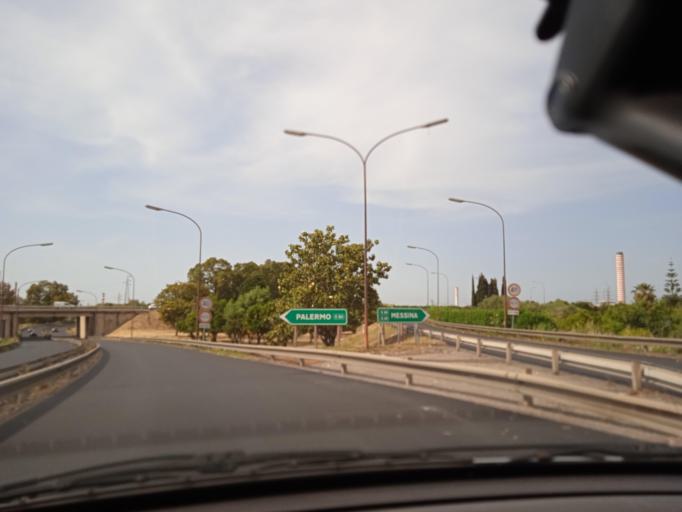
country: IT
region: Sicily
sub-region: Messina
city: San Filippo del Mela
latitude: 38.1906
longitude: 15.2747
